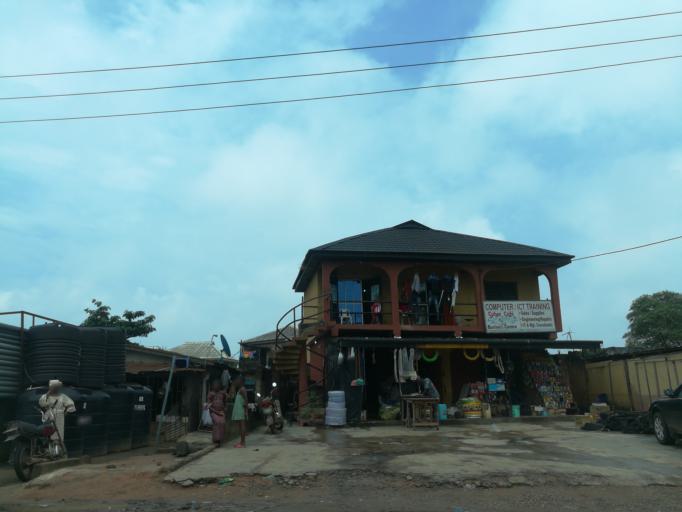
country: NG
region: Lagos
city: Ikorodu
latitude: 6.6645
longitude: 3.5183
